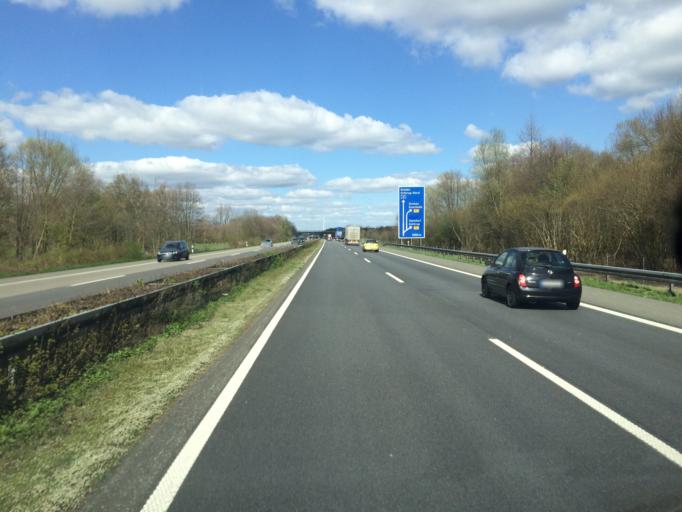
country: DE
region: North Rhine-Westphalia
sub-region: Regierungsbezirk Munster
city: Heek
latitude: 52.1771
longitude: 7.1059
